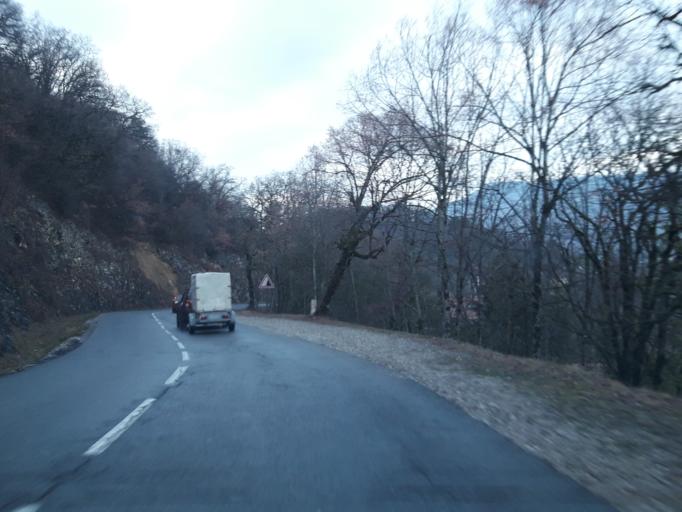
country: FR
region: Rhone-Alpes
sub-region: Departement de la Haute-Savoie
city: Monnetier-Mornex
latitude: 46.1598
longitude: 6.2243
